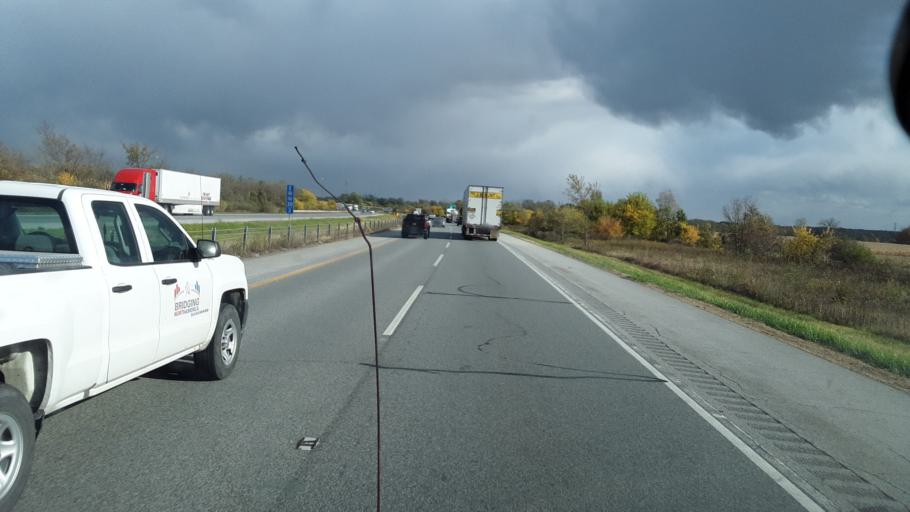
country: US
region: Indiana
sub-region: Porter County
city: Chesterton
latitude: 41.5763
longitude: -87.0651
